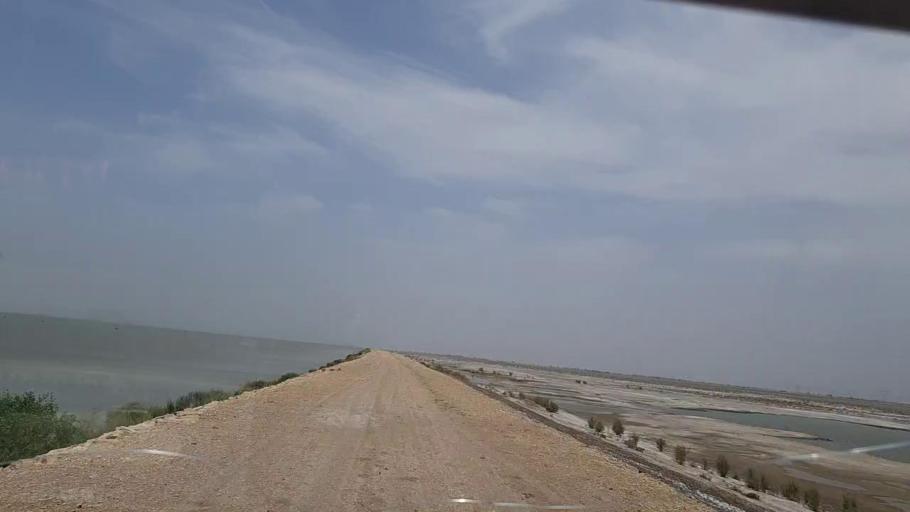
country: PK
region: Sindh
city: Sehwan
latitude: 26.4116
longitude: 67.7909
